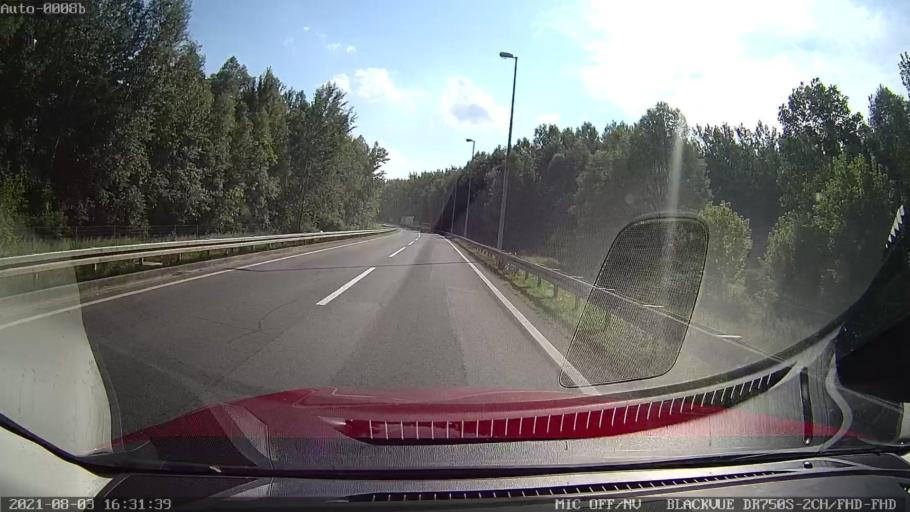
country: HR
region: Osjecko-Baranjska
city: Visnjevac
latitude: 45.5708
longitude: 18.6339
